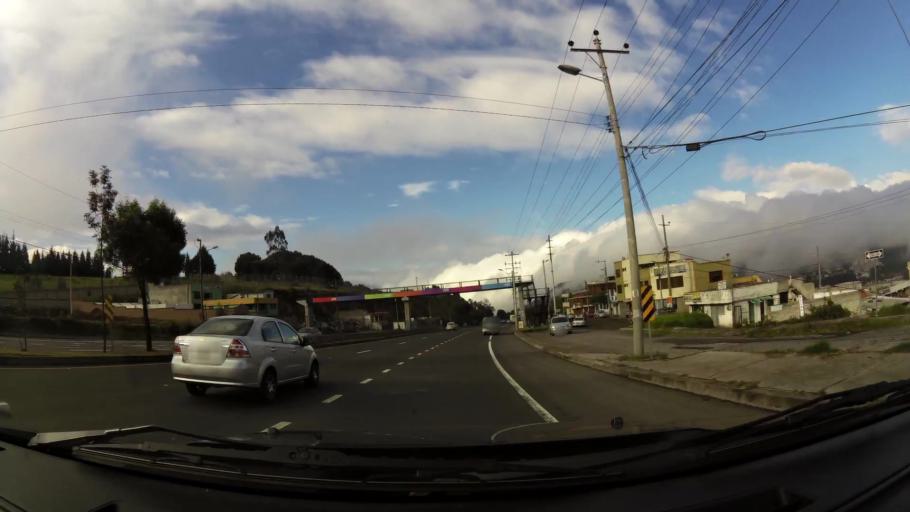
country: EC
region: Pichincha
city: Quito
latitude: -0.2402
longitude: -78.4937
